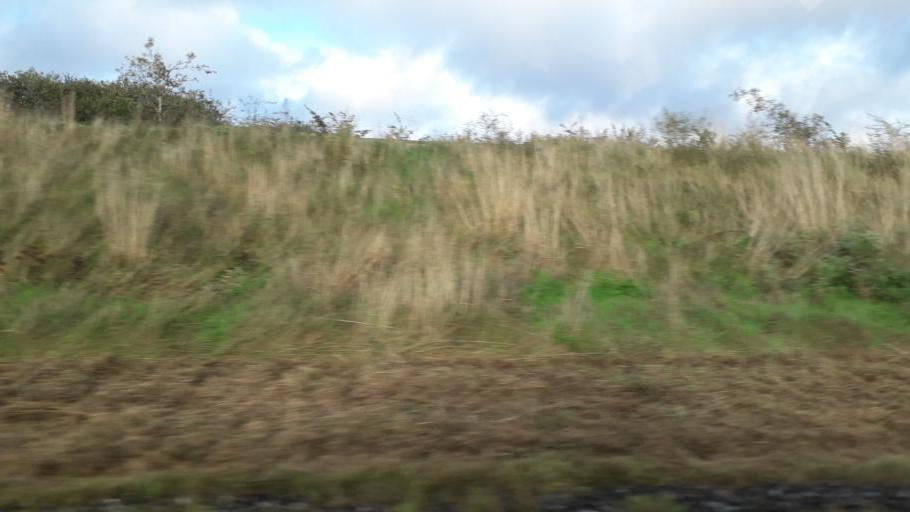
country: IE
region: Connaught
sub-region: Roscommon
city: Ballaghaderreen
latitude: 53.8994
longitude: -8.5340
